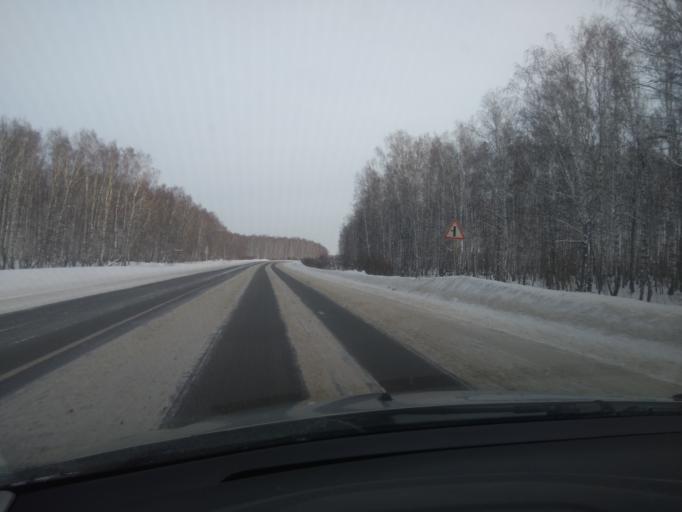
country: RU
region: Sverdlovsk
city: Bogdanovich
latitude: 56.7916
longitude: 62.0013
